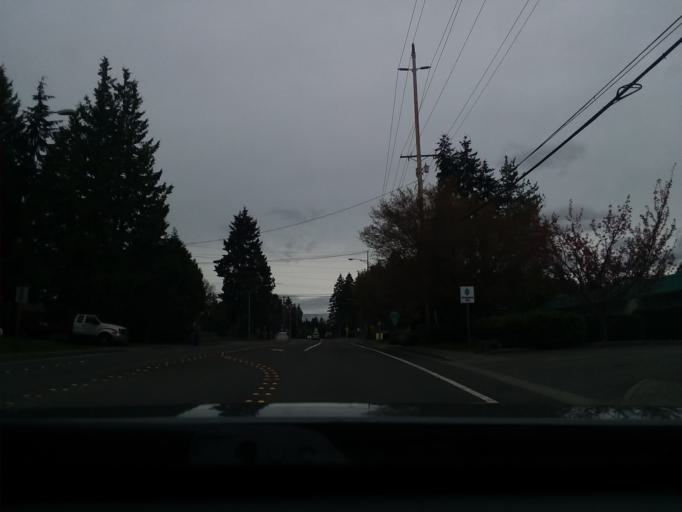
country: US
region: Washington
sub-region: Snohomish County
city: Lynnwood
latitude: 47.8093
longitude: -122.3031
